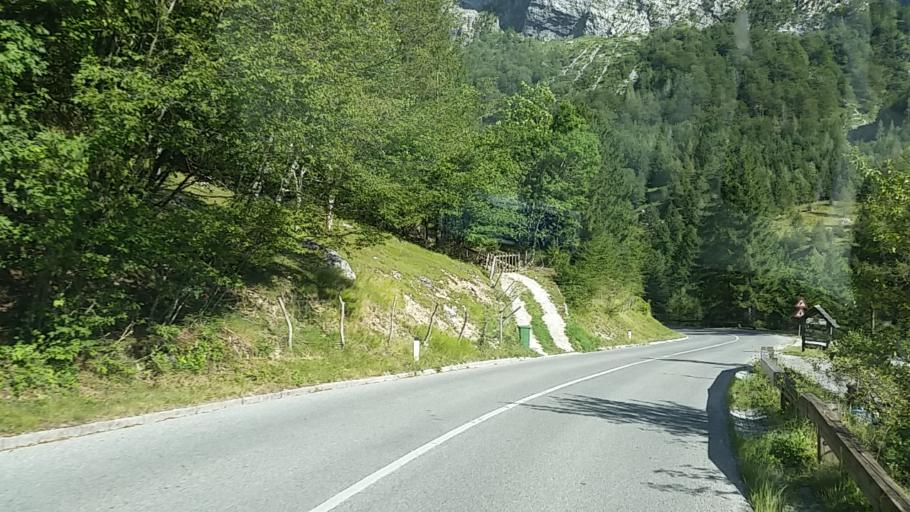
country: SI
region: Kranjska Gora
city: Kranjska Gora
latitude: 46.3833
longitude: 13.7566
